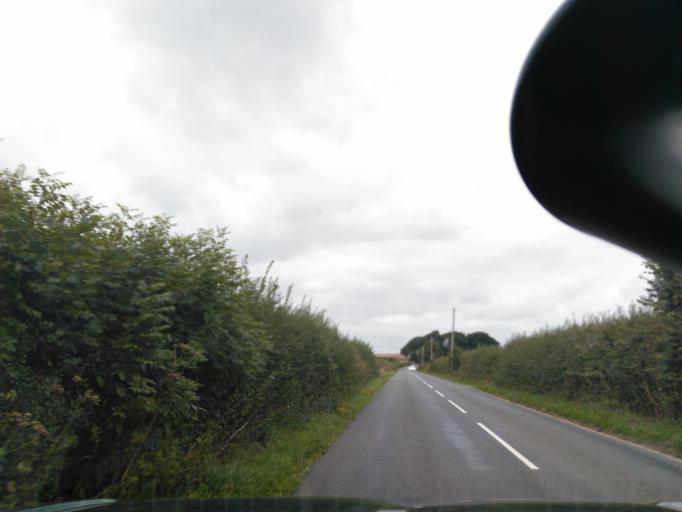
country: GB
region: England
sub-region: Dorset
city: Lytchett Matravers
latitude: 50.7353
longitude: -2.1181
